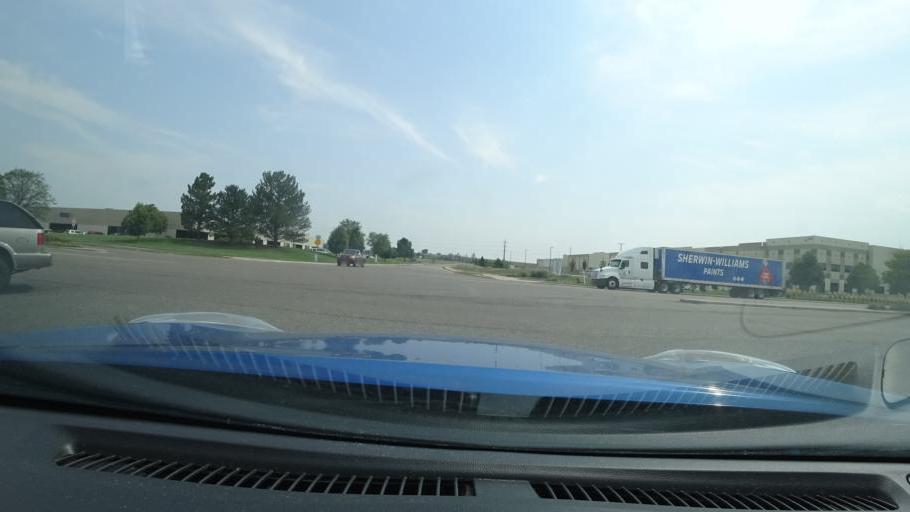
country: US
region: Colorado
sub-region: Adams County
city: Aurora
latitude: 39.7591
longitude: -104.7531
